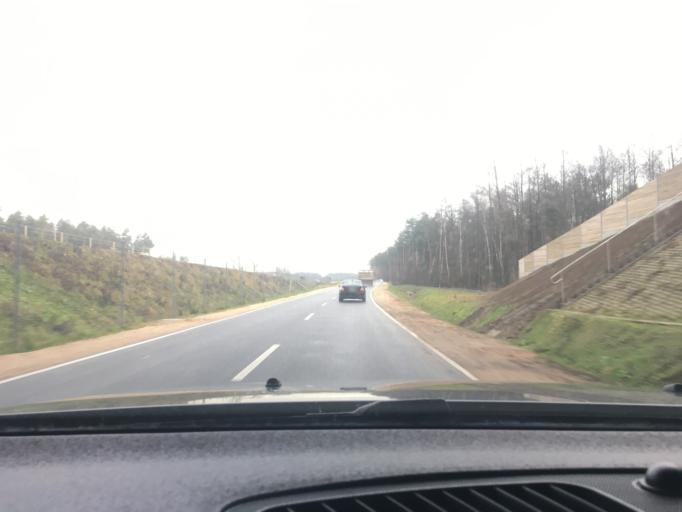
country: PL
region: Swietokrzyskie
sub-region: Powiat jedrzejowski
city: Jedrzejow
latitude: 50.6783
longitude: 20.3515
